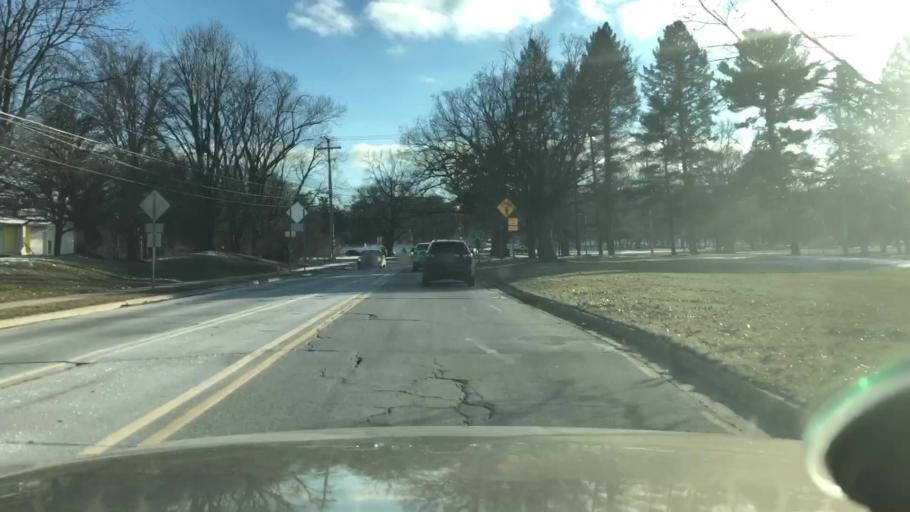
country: US
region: Michigan
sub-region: Jackson County
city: Jackson
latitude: 42.2191
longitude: -84.4183
